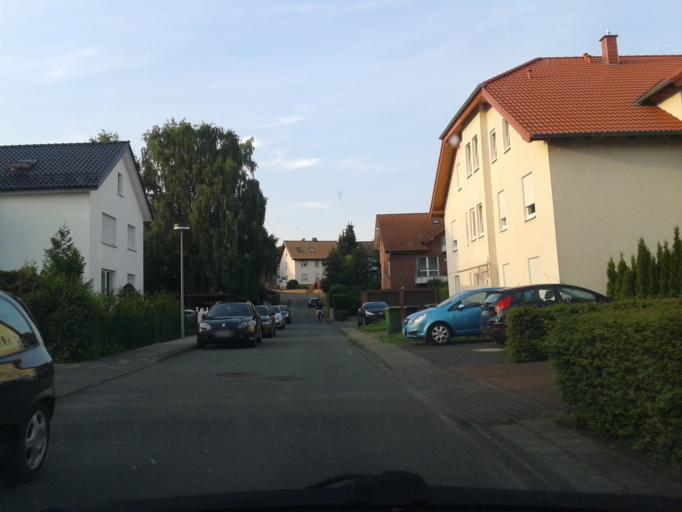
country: DE
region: North Rhine-Westphalia
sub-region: Regierungsbezirk Detmold
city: Paderborn
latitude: 51.7325
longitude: 8.6796
